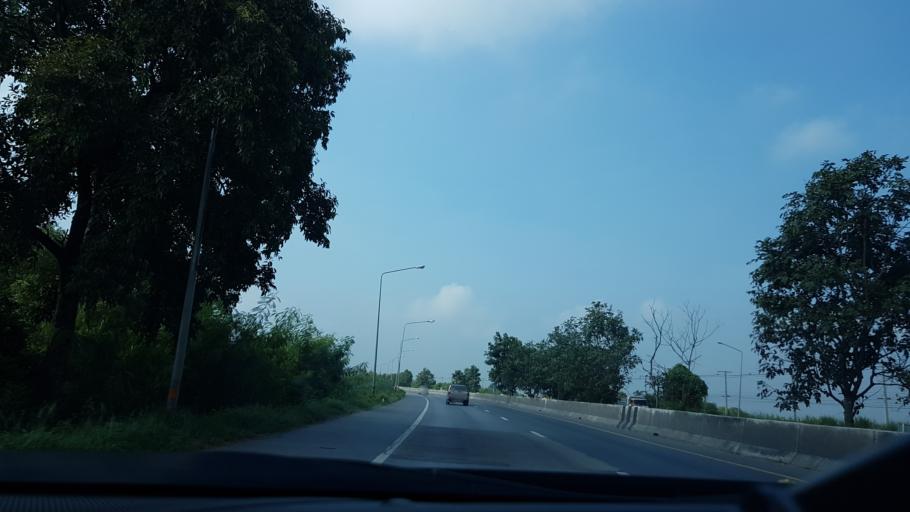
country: TH
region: Pathum Thani
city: Sam Khok
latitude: 14.1422
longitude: 100.5436
